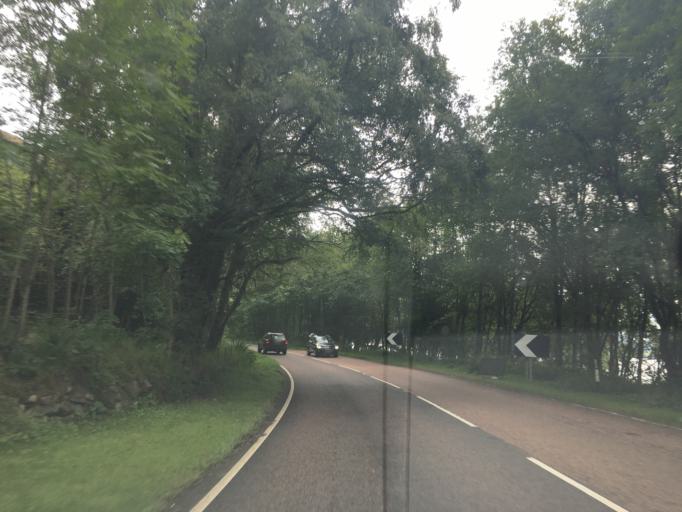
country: GB
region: Scotland
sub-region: Stirling
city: Callander
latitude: 56.2936
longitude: -4.2906
